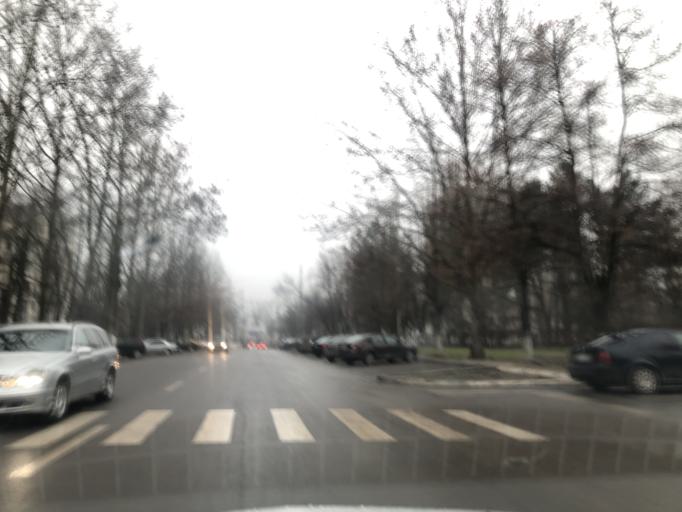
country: MD
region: Chisinau
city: Chisinau
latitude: 47.0504
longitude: 28.8588
